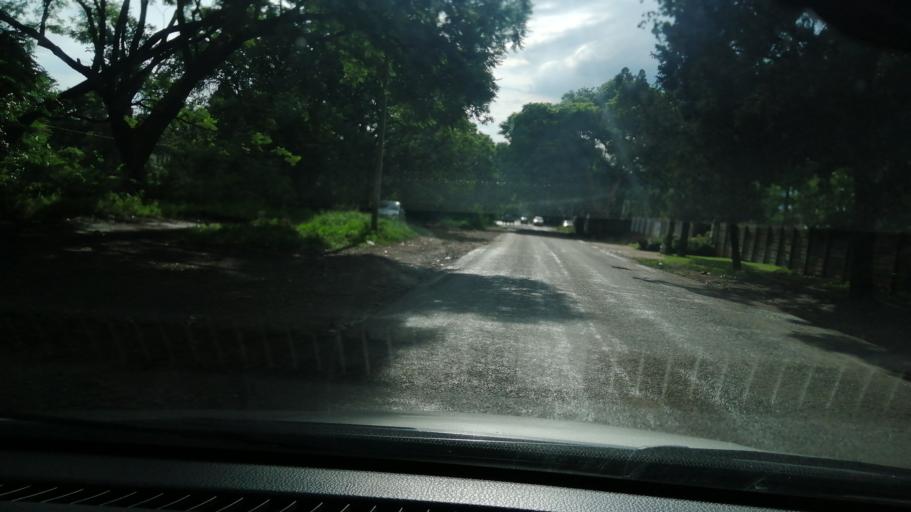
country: ZW
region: Harare
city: Harare
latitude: -17.8071
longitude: 31.0418
